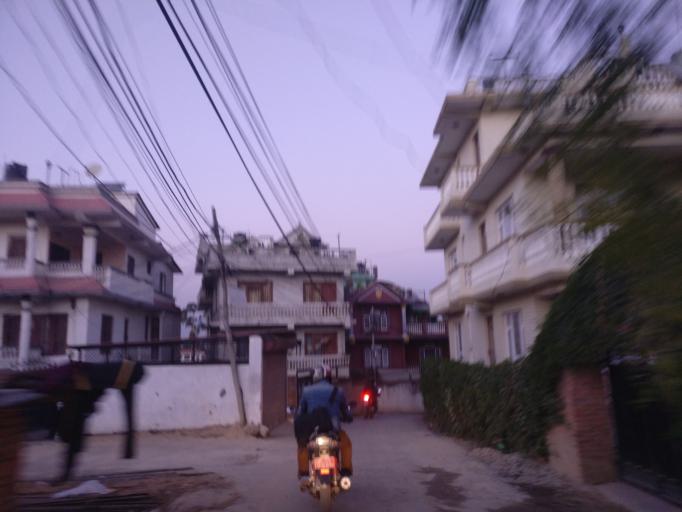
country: NP
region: Central Region
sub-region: Bagmati Zone
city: Patan
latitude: 27.6491
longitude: 85.3246
